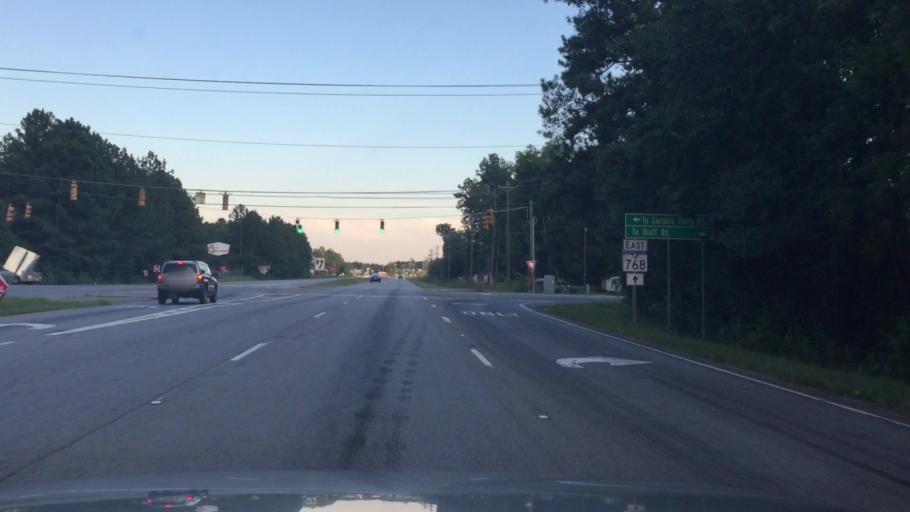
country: US
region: South Carolina
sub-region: Richland County
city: Forest Acres
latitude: 33.9486
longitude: -80.9658
